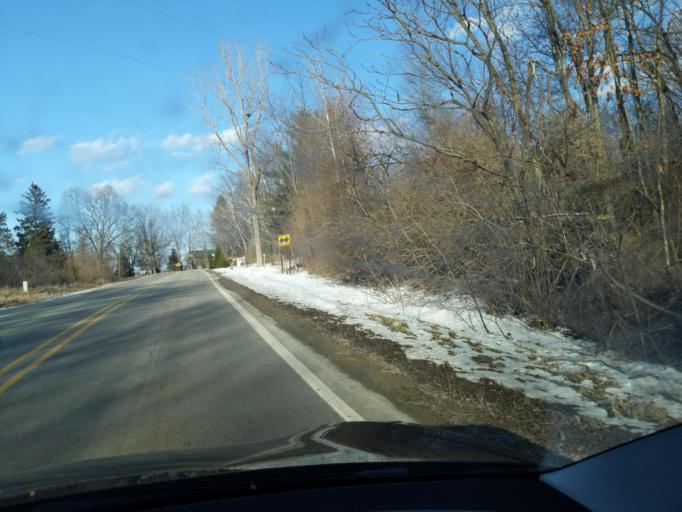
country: US
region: Michigan
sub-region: Ingham County
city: Stockbridge
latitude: 42.5244
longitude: -84.0691
